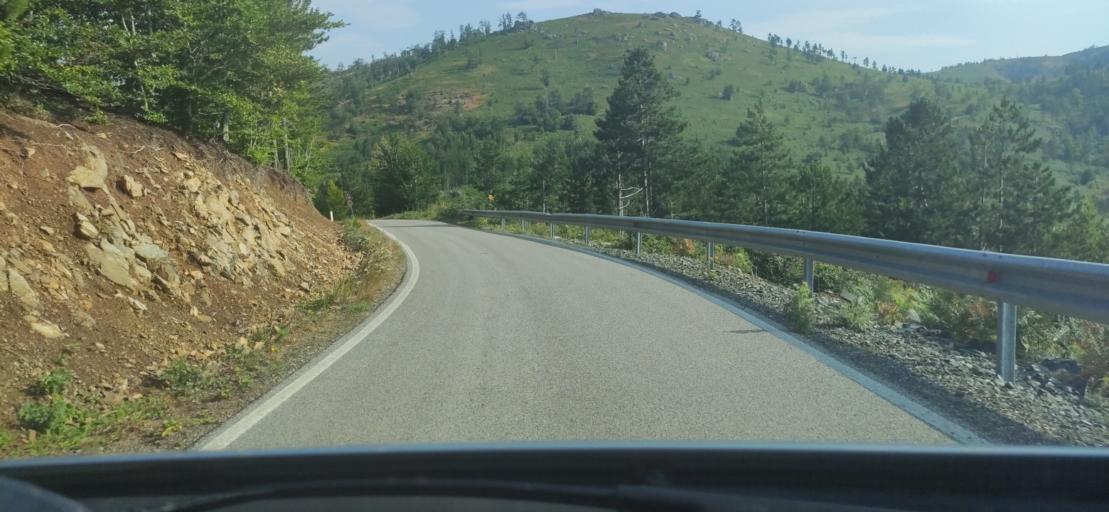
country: AL
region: Shkoder
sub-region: Rrethi i Pukes
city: Iballe
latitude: 42.1738
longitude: 20.0257
